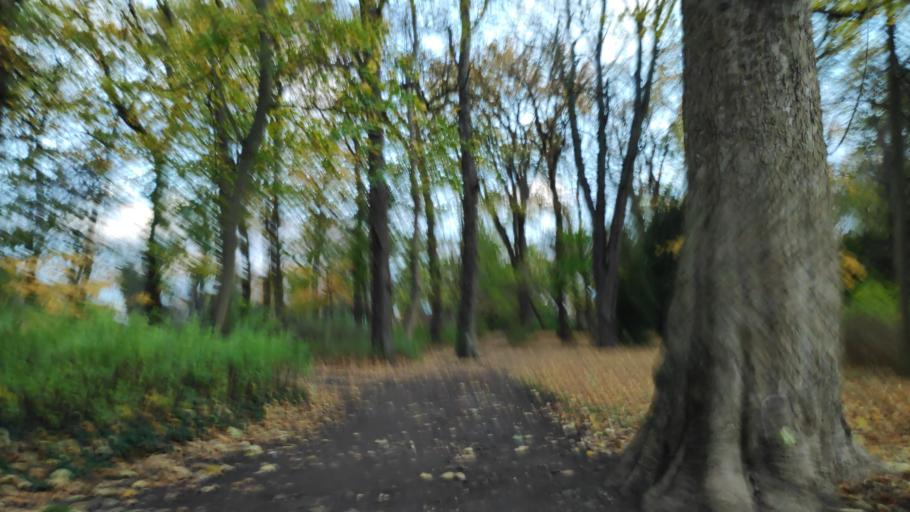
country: DE
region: North Rhine-Westphalia
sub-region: Regierungsbezirk Detmold
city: Minden
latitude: 52.2837
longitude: 8.9167
